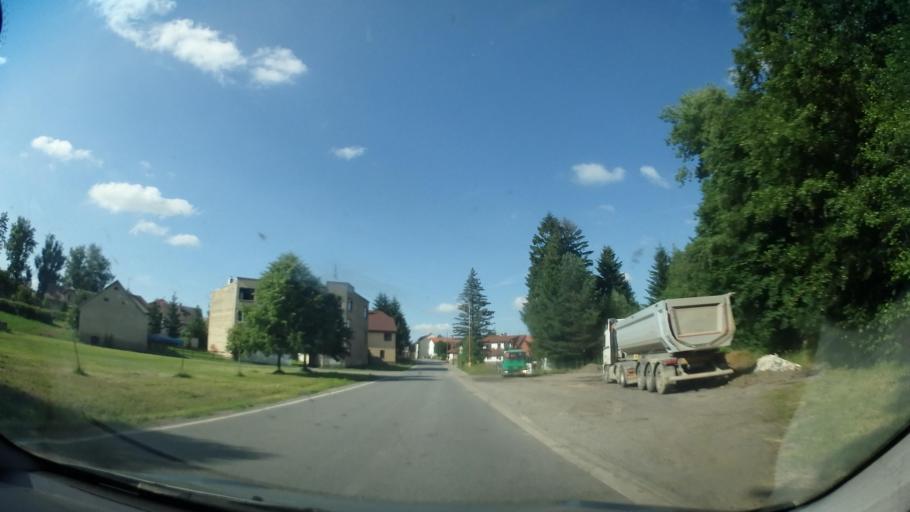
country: CZ
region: Vysocina
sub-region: Okres Zd'ar nad Sazavou
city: Svratka
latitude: 49.7183
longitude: 16.0346
